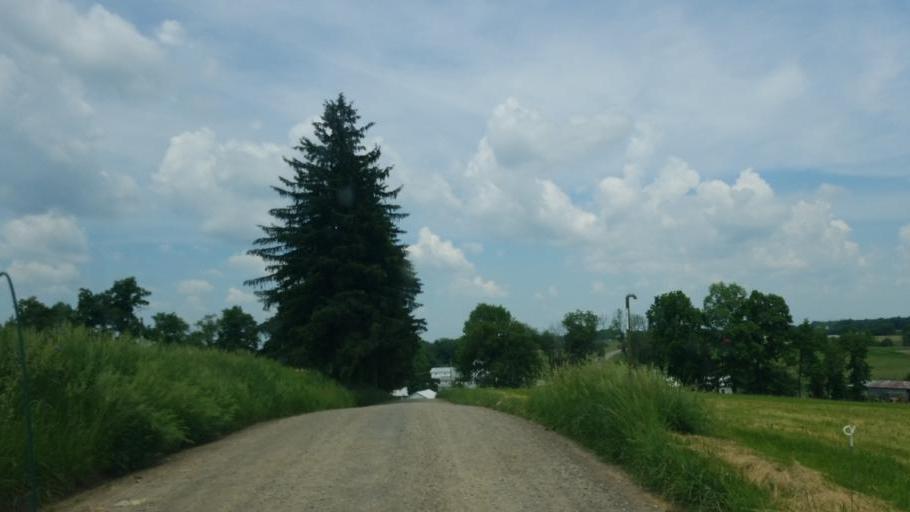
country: US
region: Ohio
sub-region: Coshocton County
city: West Lafayette
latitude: 40.4228
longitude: -81.7888
